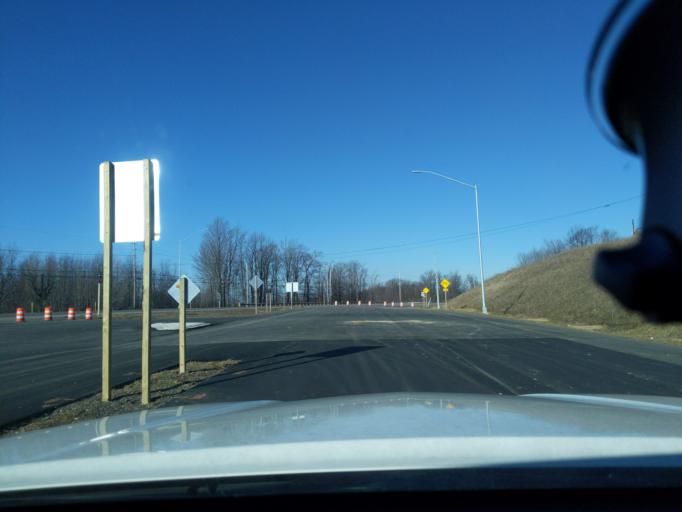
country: US
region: Pennsylvania
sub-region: Somerset County
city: Meyersdale
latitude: 39.7043
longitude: -79.0964
